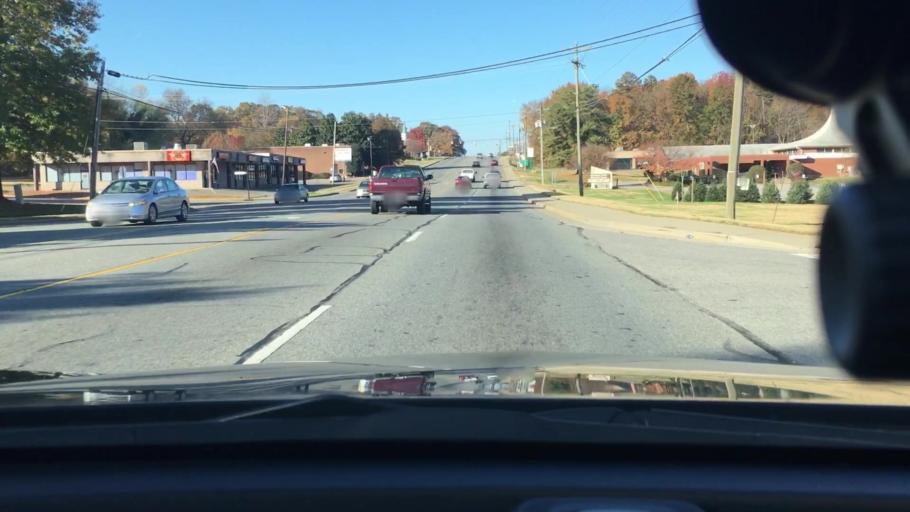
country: US
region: North Carolina
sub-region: Cabarrus County
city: Harrisburg
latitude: 35.3221
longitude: -80.6513
